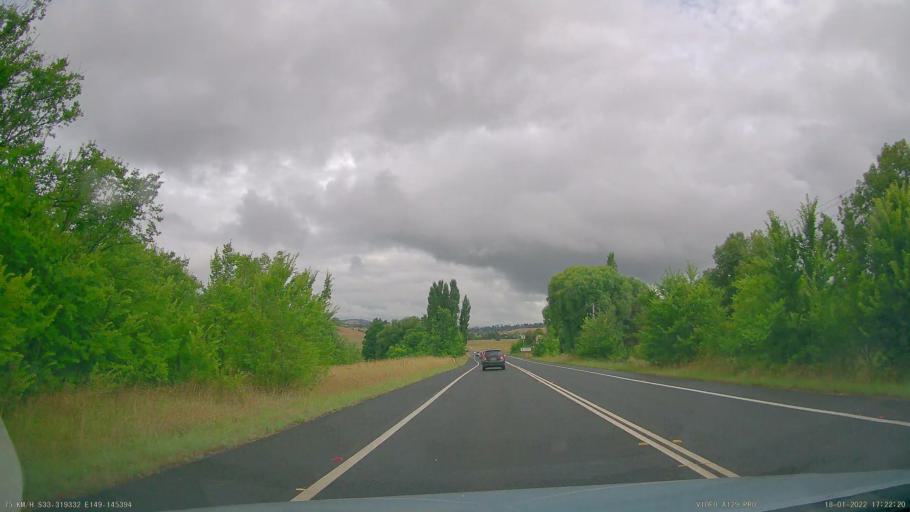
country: AU
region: New South Wales
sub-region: Orange Municipality
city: Orange
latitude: -33.3195
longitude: 149.1455
